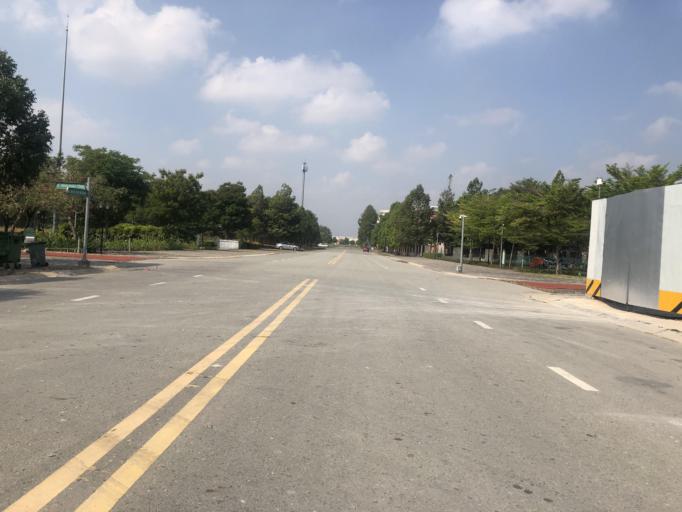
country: VN
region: Binh Duong
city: Thu Dau Mot
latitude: 11.0692
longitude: 106.6787
